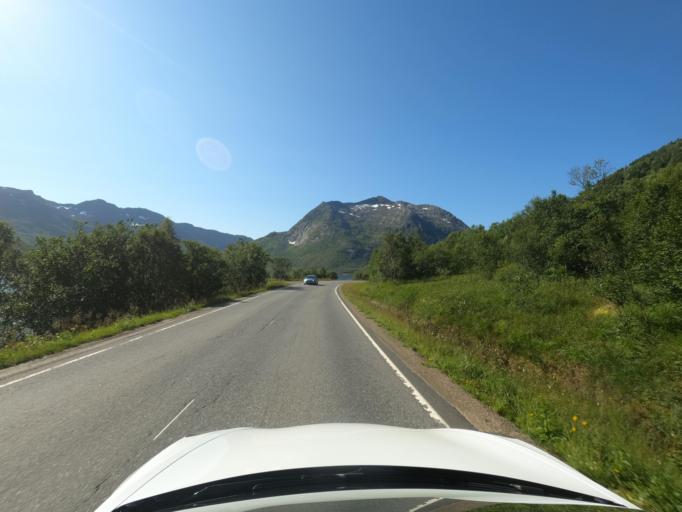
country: NO
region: Nordland
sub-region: Lodingen
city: Lodingen
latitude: 68.5475
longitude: 15.7442
